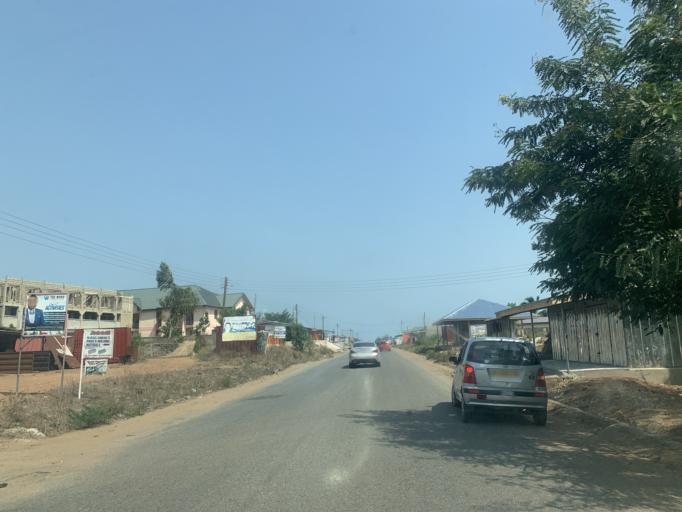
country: GH
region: Central
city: Winneba
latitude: 5.3991
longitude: -0.6501
